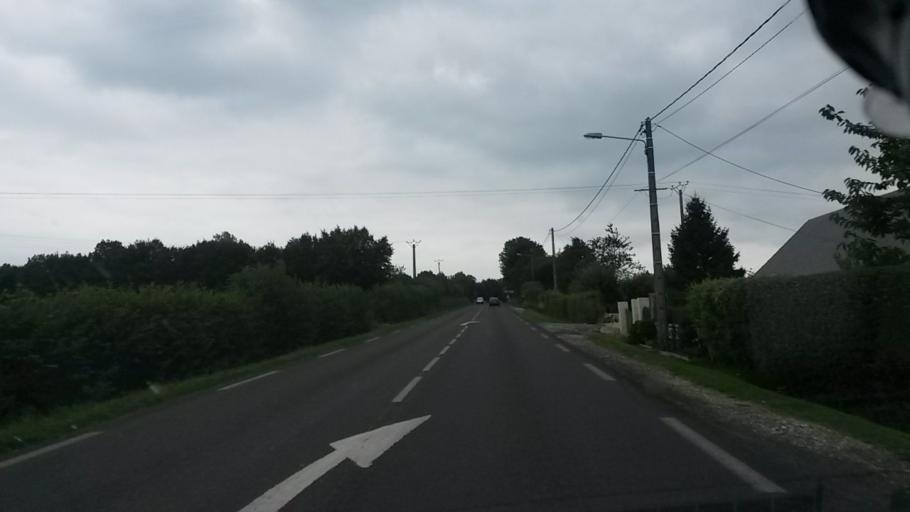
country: FR
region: Haute-Normandie
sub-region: Departement de la Seine-Maritime
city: Gaillefontaine
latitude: 49.6411
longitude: 1.6138
